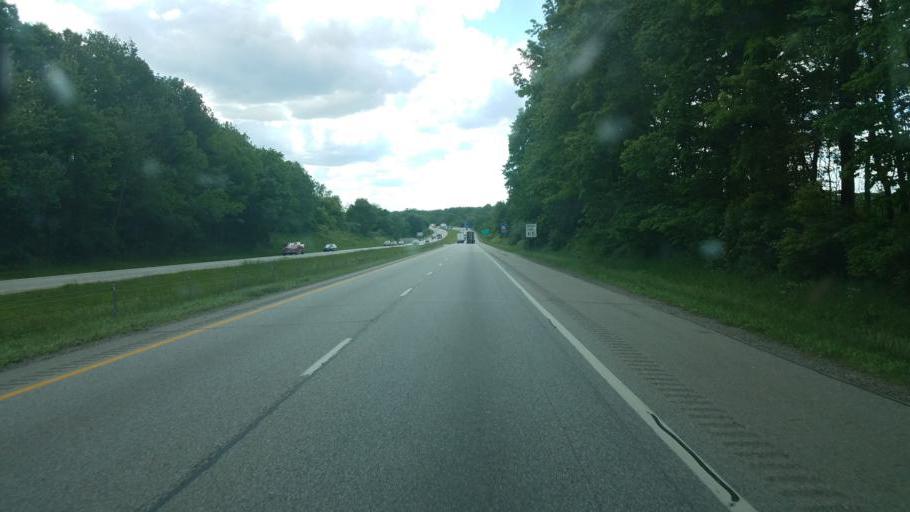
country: US
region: Ohio
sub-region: Portage County
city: Brimfield
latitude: 41.1070
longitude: -81.3589
